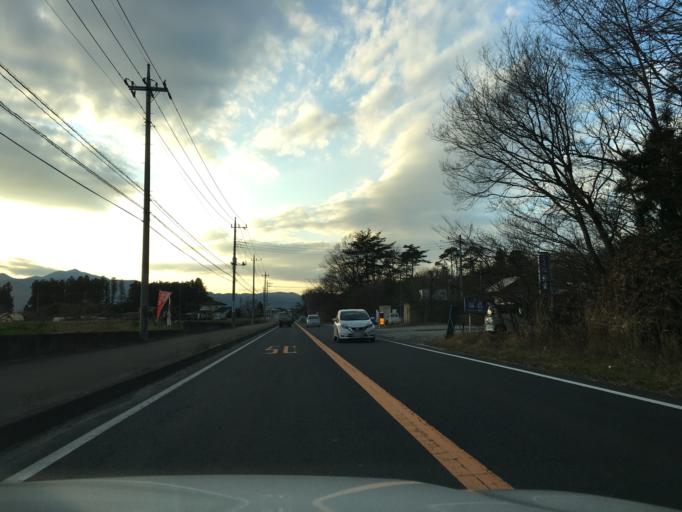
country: JP
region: Tochigi
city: Otawara
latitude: 36.9158
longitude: 139.9621
